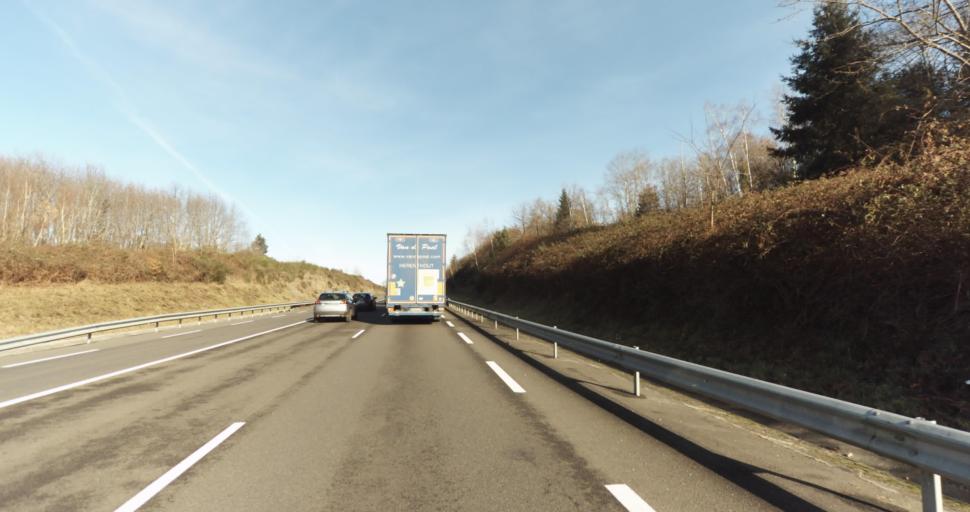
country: FR
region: Limousin
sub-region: Departement de la Haute-Vienne
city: Aixe-sur-Vienne
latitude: 45.8387
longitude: 1.1490
